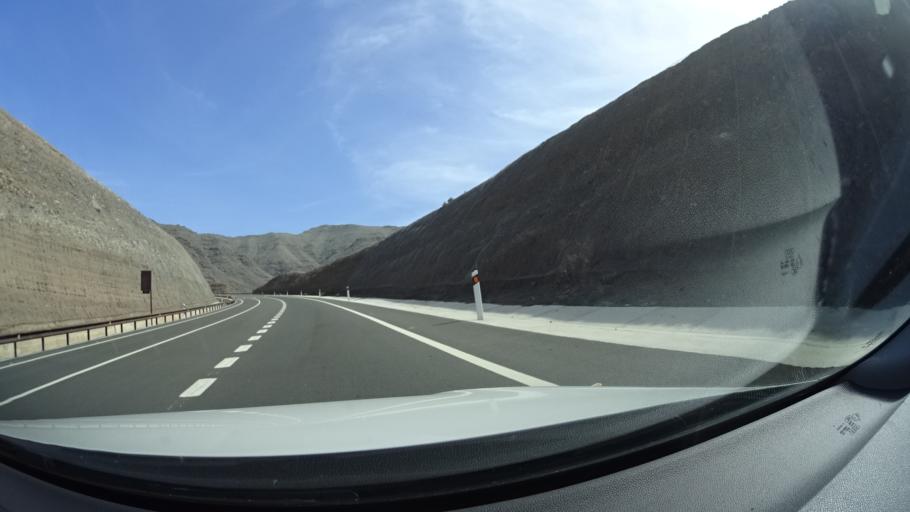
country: ES
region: Canary Islands
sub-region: Provincia de Las Palmas
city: San Nicolas
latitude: 28.0133
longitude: -15.7732
